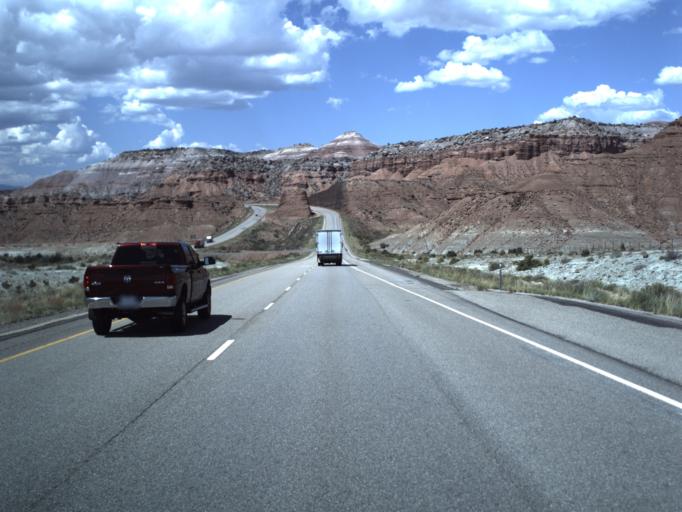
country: US
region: Utah
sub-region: Emery County
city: Ferron
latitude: 38.8312
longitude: -111.1213
